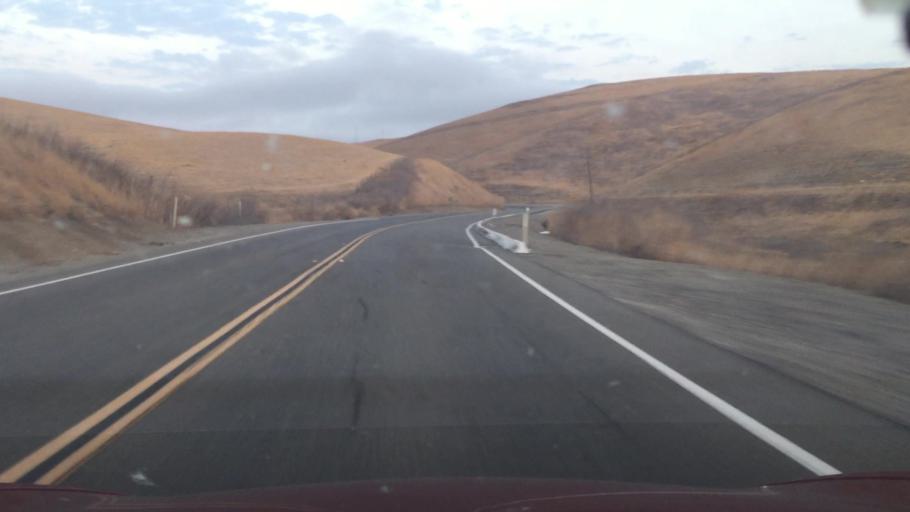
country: US
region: California
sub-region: San Joaquin County
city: Mountain House
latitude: 37.7442
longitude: -121.6275
